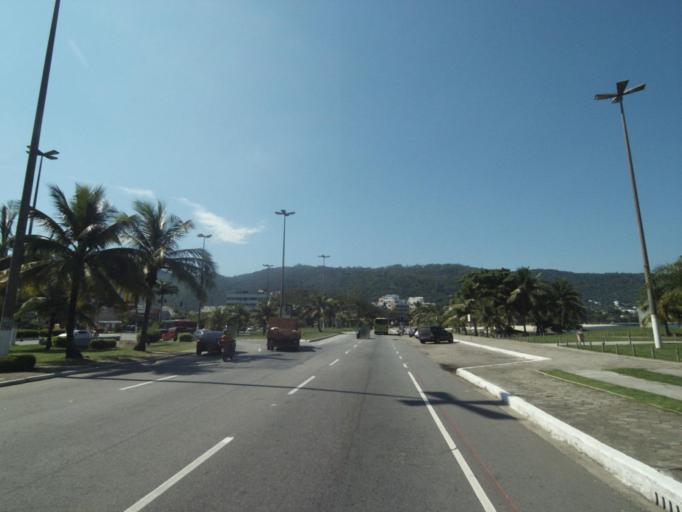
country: BR
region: Rio de Janeiro
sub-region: Niteroi
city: Niteroi
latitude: -22.9146
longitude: -43.0966
